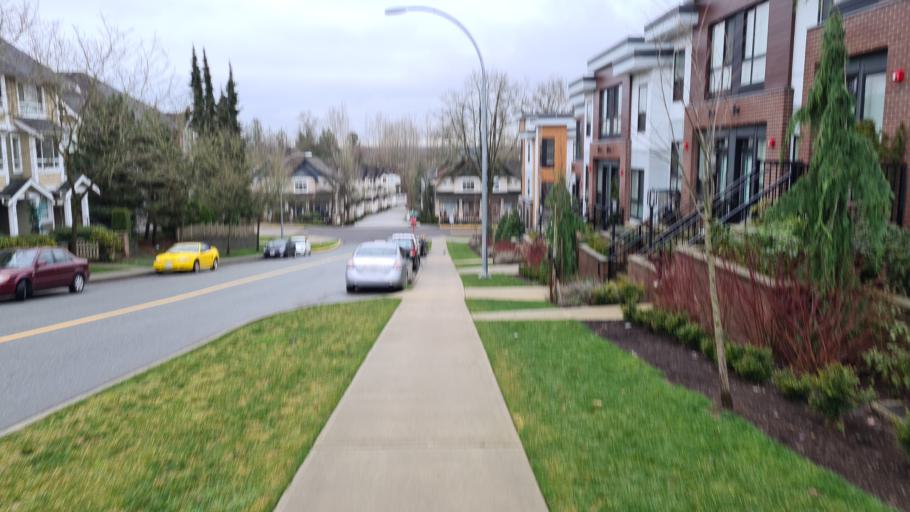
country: CA
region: British Columbia
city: Langley
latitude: 49.1270
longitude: -122.6648
